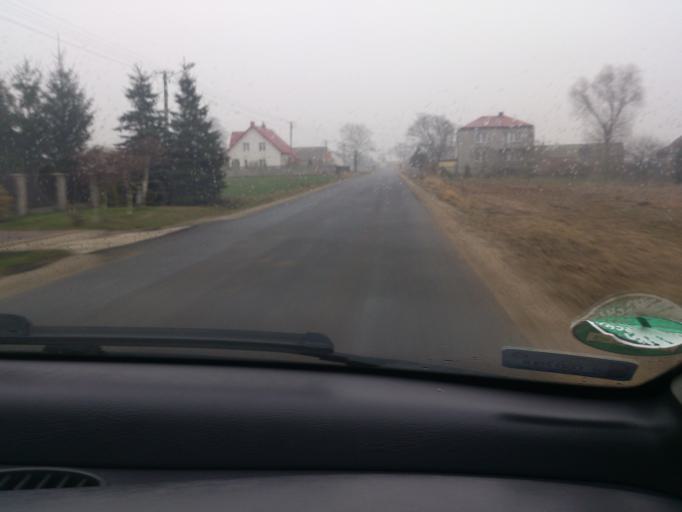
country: PL
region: Masovian Voivodeship
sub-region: Plock
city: Plock
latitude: 52.6166
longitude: 19.7441
